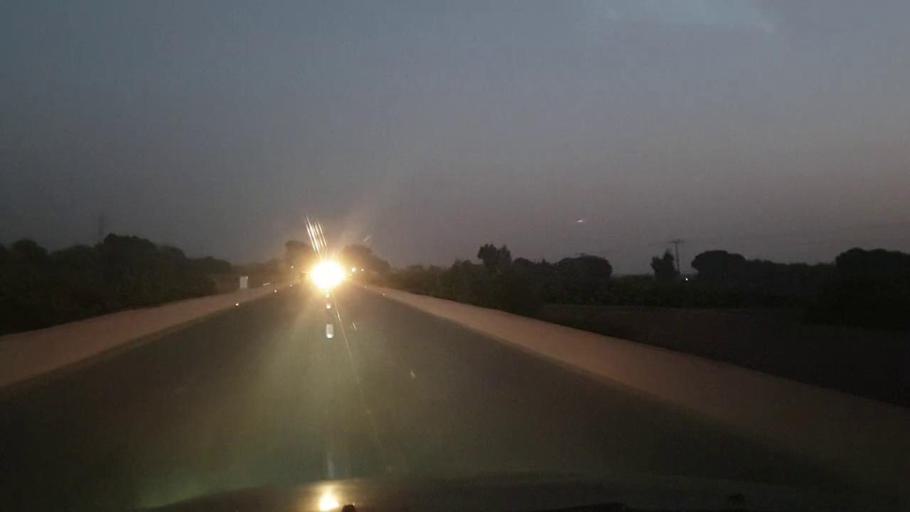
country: PK
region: Sindh
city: Tando Allahyar
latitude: 25.3836
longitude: 68.7740
